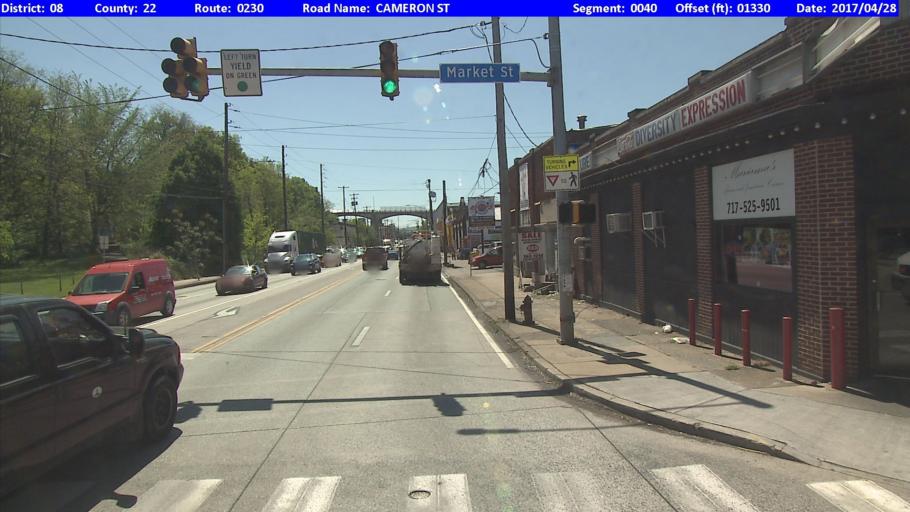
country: US
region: Pennsylvania
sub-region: Dauphin County
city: Harrisburg
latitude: 40.2644
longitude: -76.8746
